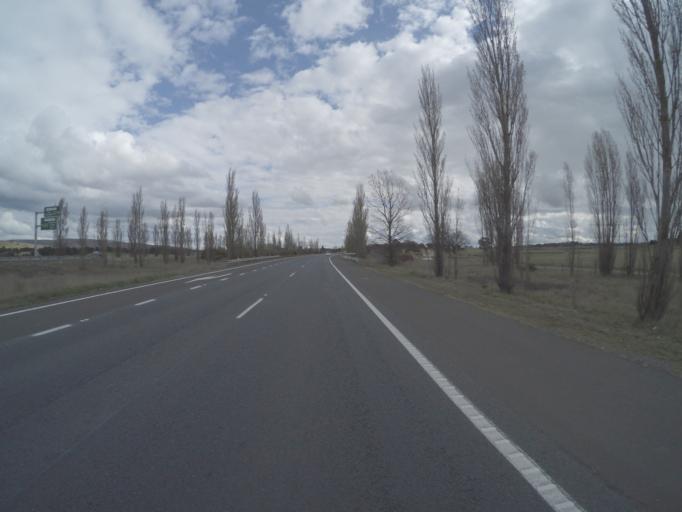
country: AU
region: New South Wales
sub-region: Goulburn Mulwaree
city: Goulburn
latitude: -34.7964
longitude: 149.6155
